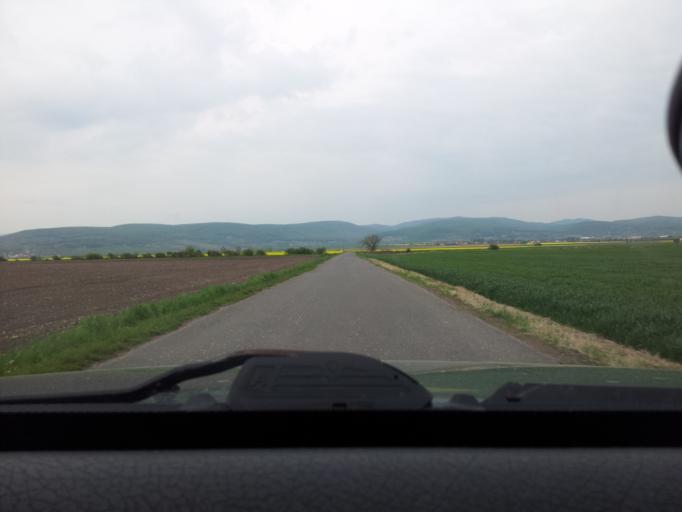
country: SK
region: Nitriansky
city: Tlmace
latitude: 48.2649
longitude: 18.5768
